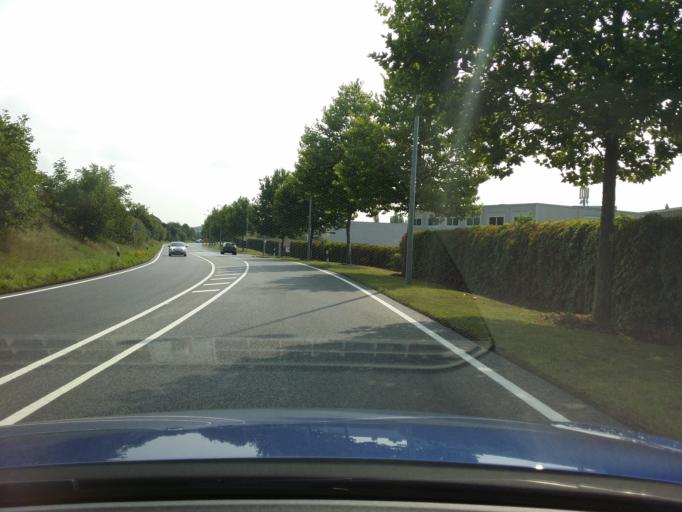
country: LU
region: Luxembourg
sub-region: Canton de Luxembourg
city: Bertrange
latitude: 49.6157
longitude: 6.0559
